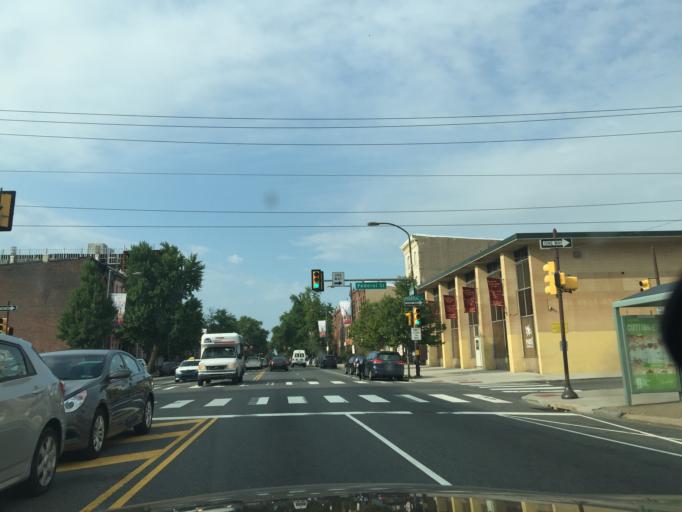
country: US
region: Pennsylvania
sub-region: Philadelphia County
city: Philadelphia
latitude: 39.9360
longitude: -75.1672
